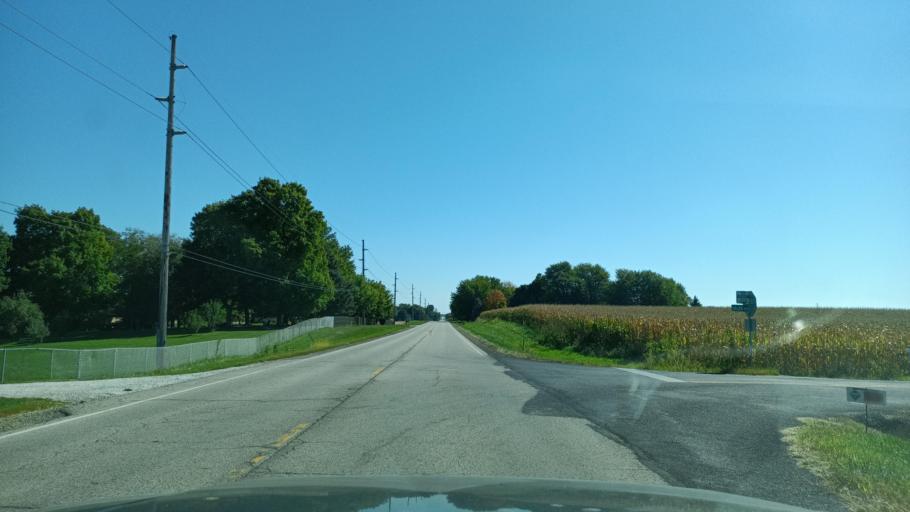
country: US
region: Illinois
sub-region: Peoria County
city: Dunlap
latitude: 40.7859
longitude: -89.7276
